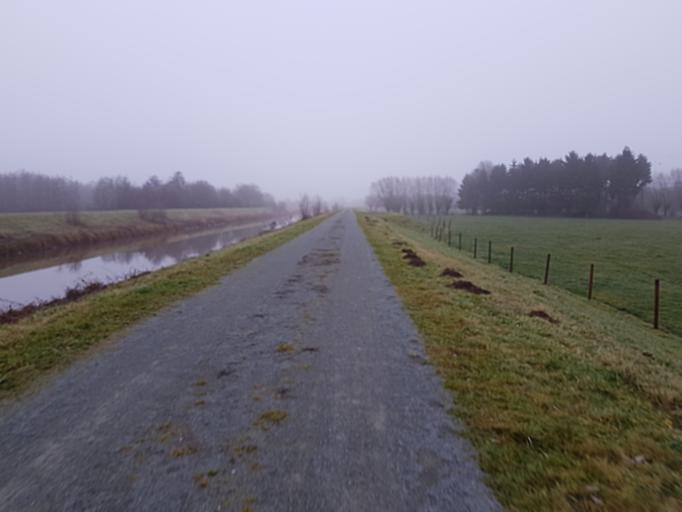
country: BE
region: Flanders
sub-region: Provincie Antwerpen
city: Bonheiden
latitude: 51.0021
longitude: 4.5464
